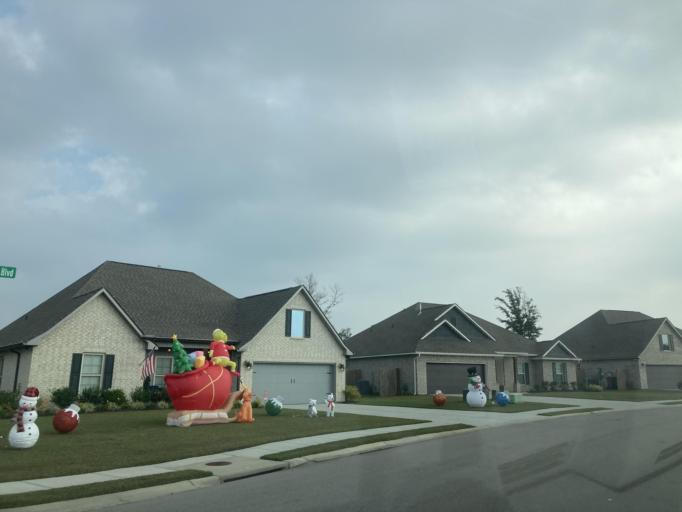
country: US
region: Mississippi
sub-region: Harrison County
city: Long Beach
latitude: 30.3734
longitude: -89.1612
